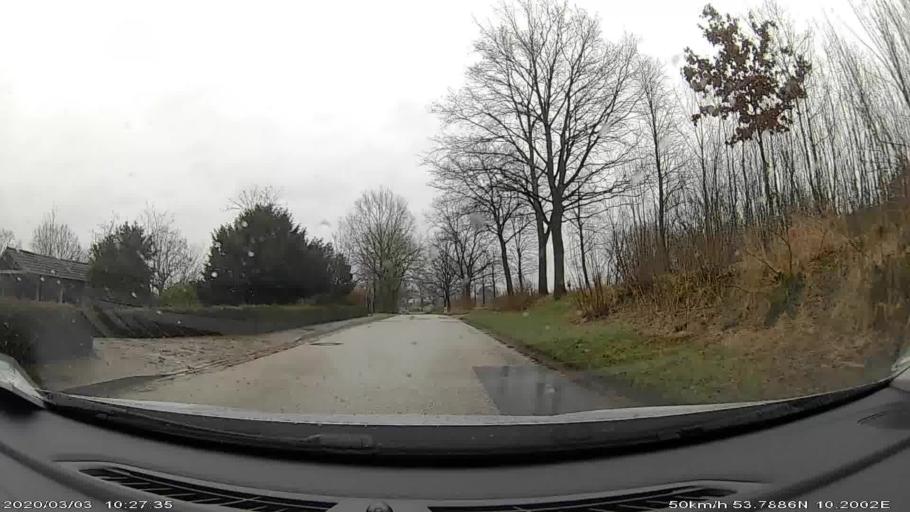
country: DE
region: Schleswig-Holstein
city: Nienwohld
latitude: 53.7896
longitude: 10.2042
